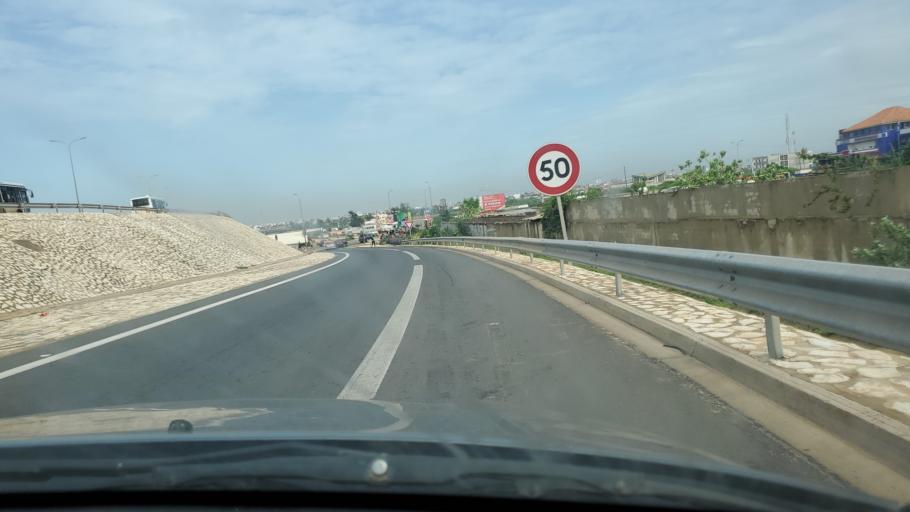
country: SN
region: Dakar
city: Pikine
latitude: 14.7457
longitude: -17.4084
